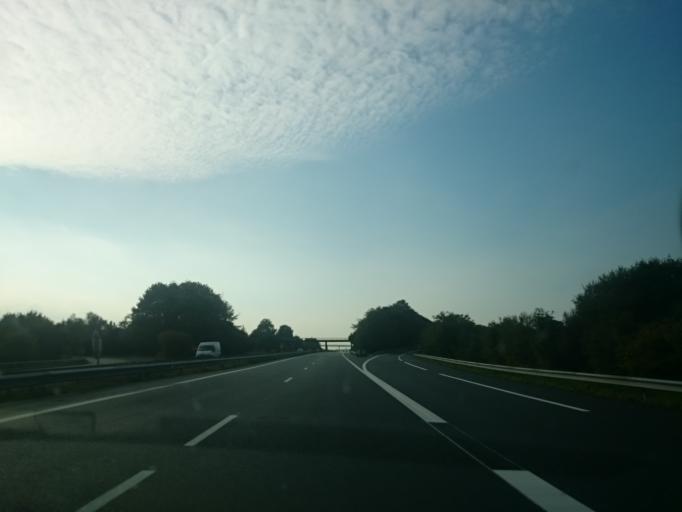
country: FR
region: Brittany
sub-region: Departement du Finistere
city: Guerlesquin
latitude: 48.5692
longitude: -3.6023
